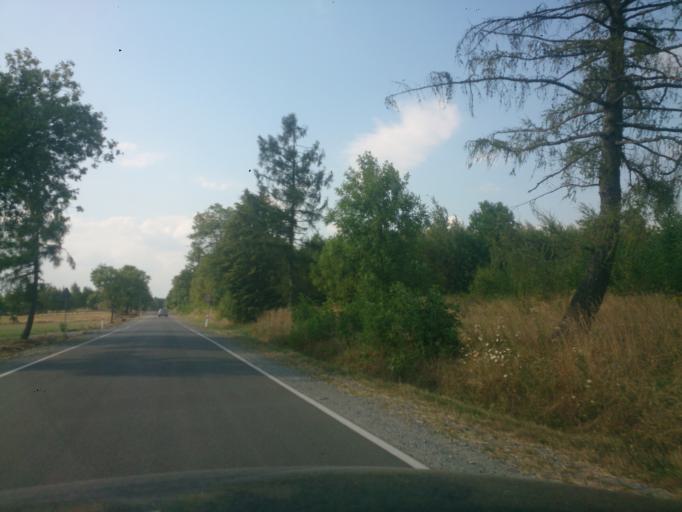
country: PL
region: Swietokrzyskie
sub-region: Powiat opatowski
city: Iwaniska
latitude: 50.6944
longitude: 21.3419
